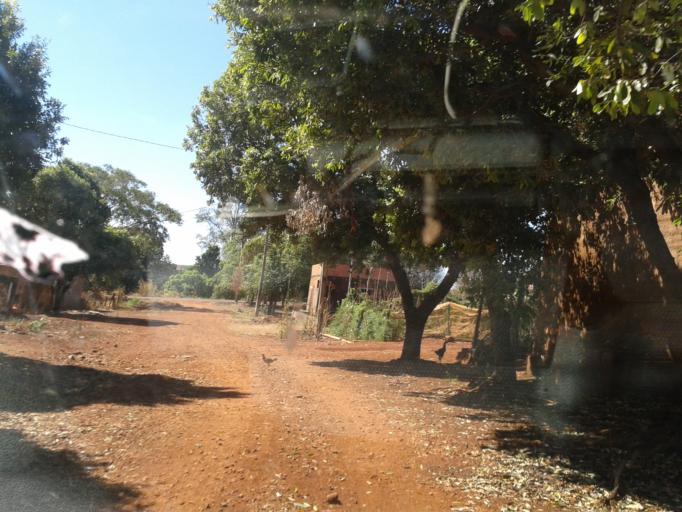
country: BR
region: Minas Gerais
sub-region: Capinopolis
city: Capinopolis
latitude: -18.6855
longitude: -49.5868
